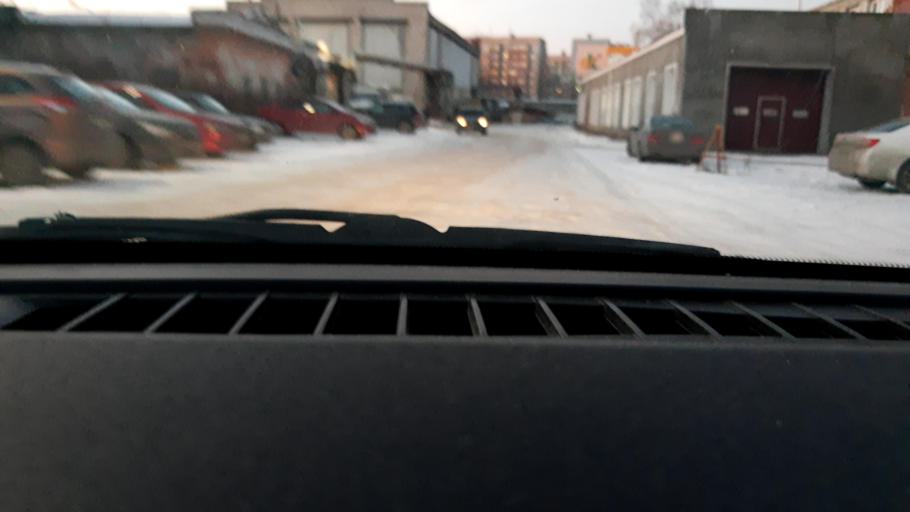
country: RU
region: Nizjnij Novgorod
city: Neklyudovo
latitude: 56.3537
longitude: 43.8742
